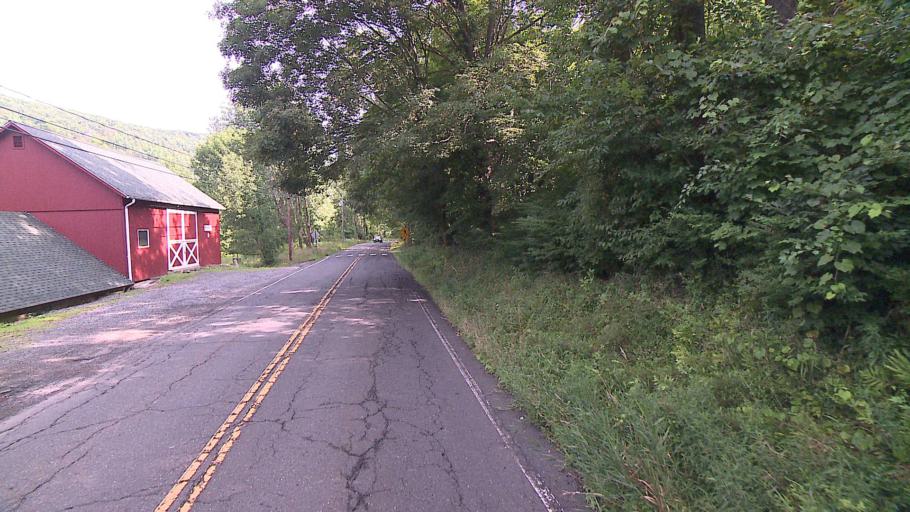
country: US
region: New York
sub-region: Putnam County
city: Putnam Lake
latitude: 41.5097
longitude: -73.5274
